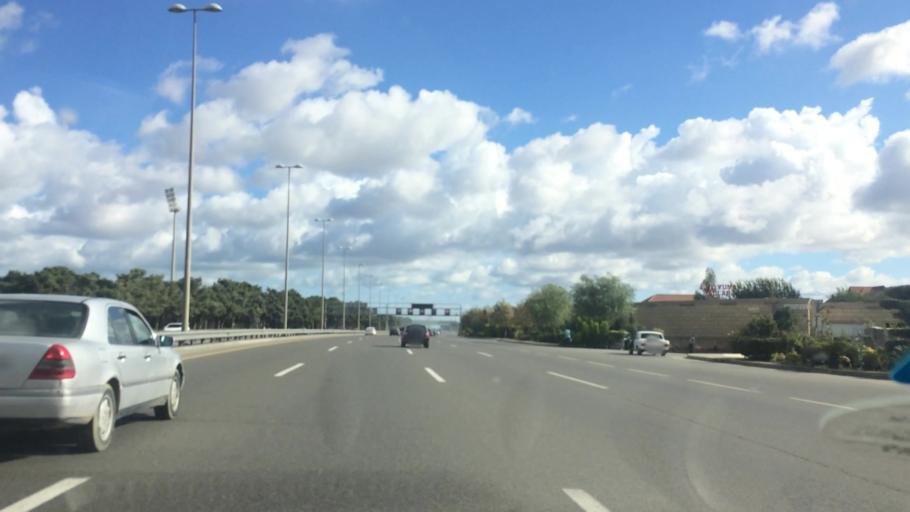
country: AZ
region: Baki
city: Biny Selo
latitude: 40.4632
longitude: 50.0831
